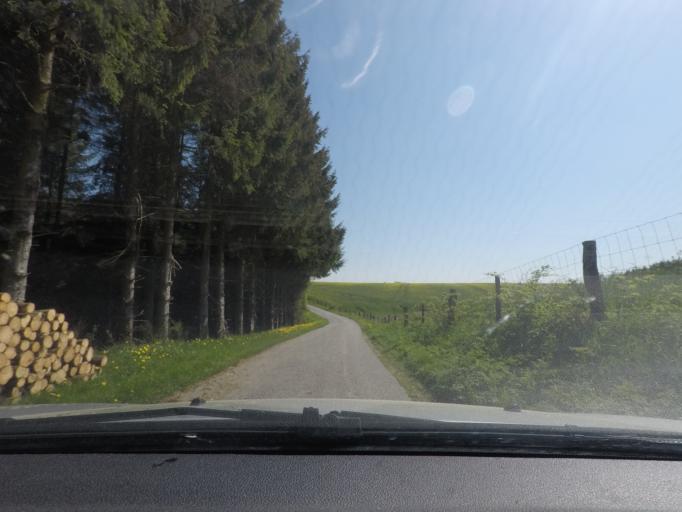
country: BE
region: Wallonia
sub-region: Province du Luxembourg
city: Leglise
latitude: 49.7882
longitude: 5.4803
